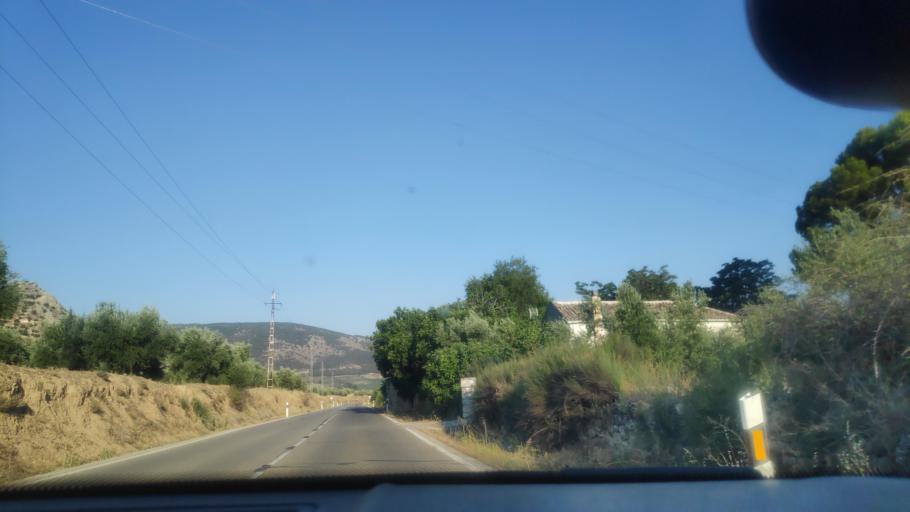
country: ES
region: Andalusia
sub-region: Provincia de Jaen
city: Jaen
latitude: 37.7473
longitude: -3.7828
